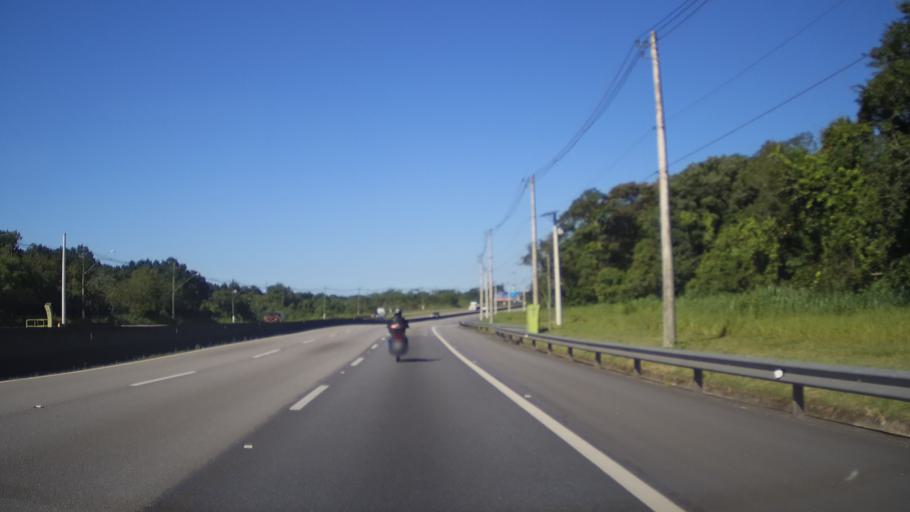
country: BR
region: Sao Paulo
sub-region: Praia Grande
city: Praia Grande
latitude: -23.9661
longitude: -46.4718
